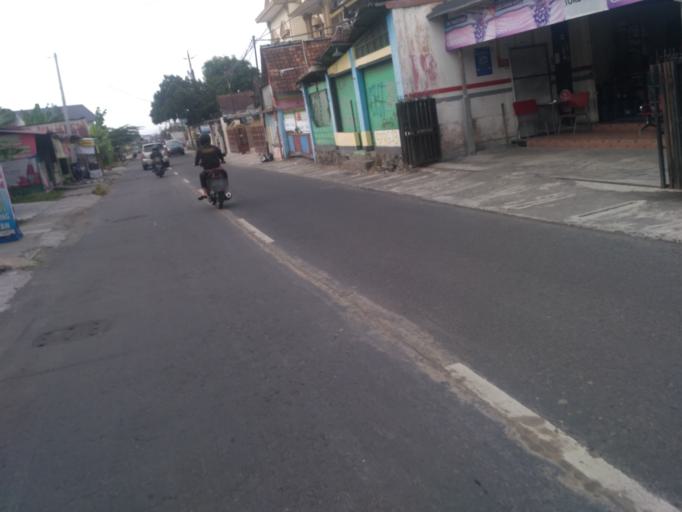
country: ID
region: Daerah Istimewa Yogyakarta
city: Yogyakarta
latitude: -7.7697
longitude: 110.3569
